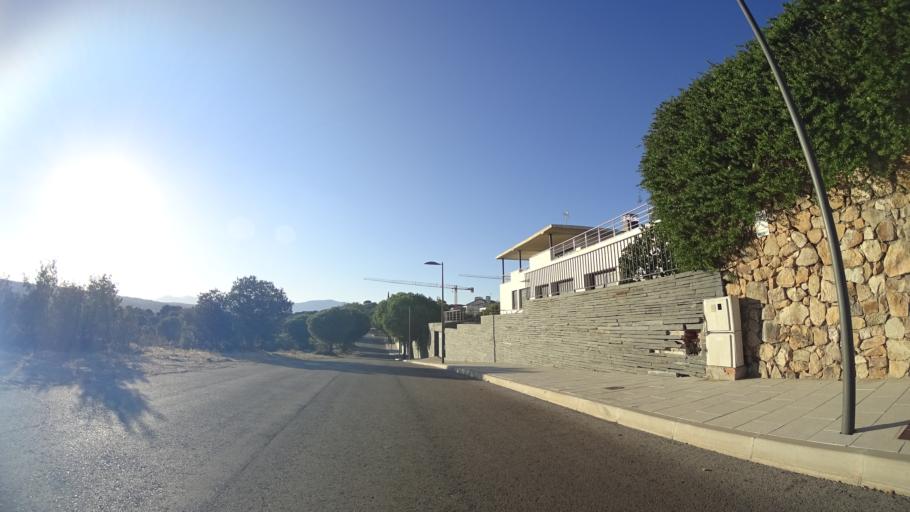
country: ES
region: Madrid
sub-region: Provincia de Madrid
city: Torrelodones
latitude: 40.5715
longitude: -3.9360
